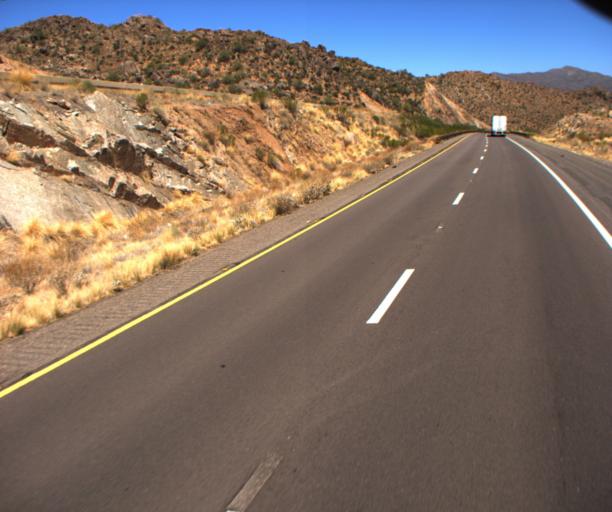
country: US
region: Arizona
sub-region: Maricopa County
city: Rio Verde
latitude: 33.7006
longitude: -111.5026
